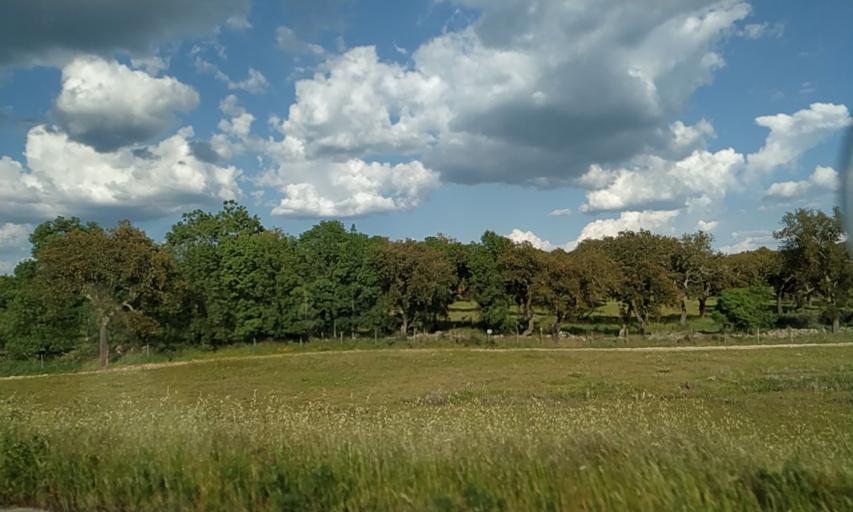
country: PT
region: Portalegre
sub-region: Portalegre
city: Urra
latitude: 39.2200
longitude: -7.4576
